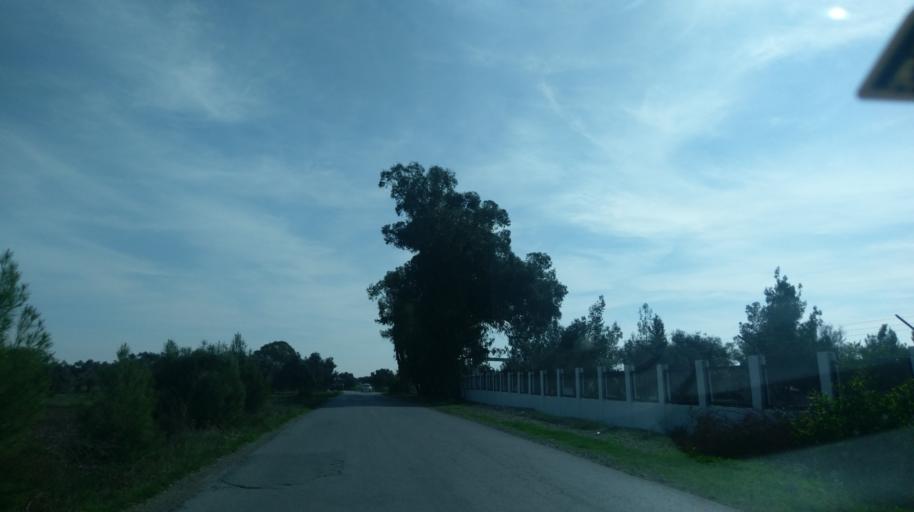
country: CY
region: Larnaka
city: Athienou
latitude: 35.1570
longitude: 33.6195
